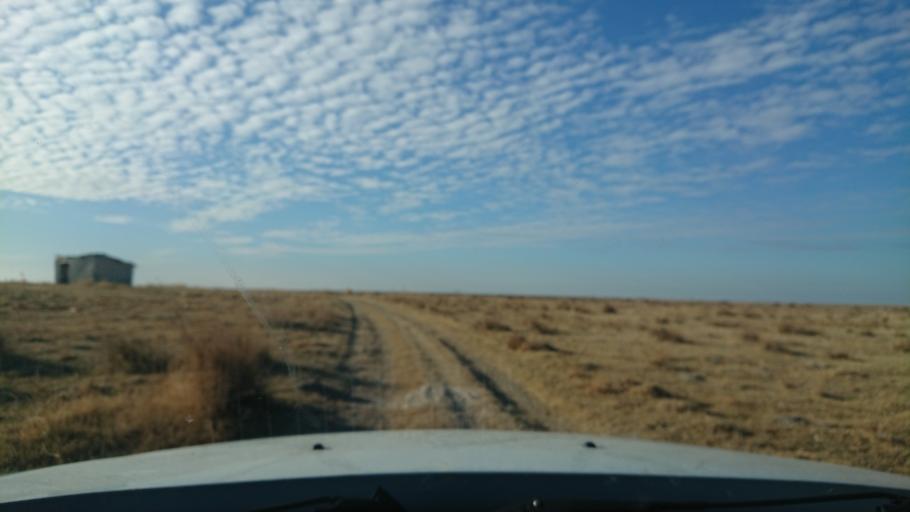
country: TR
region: Aksaray
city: Eskil
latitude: 38.5457
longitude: 33.3205
